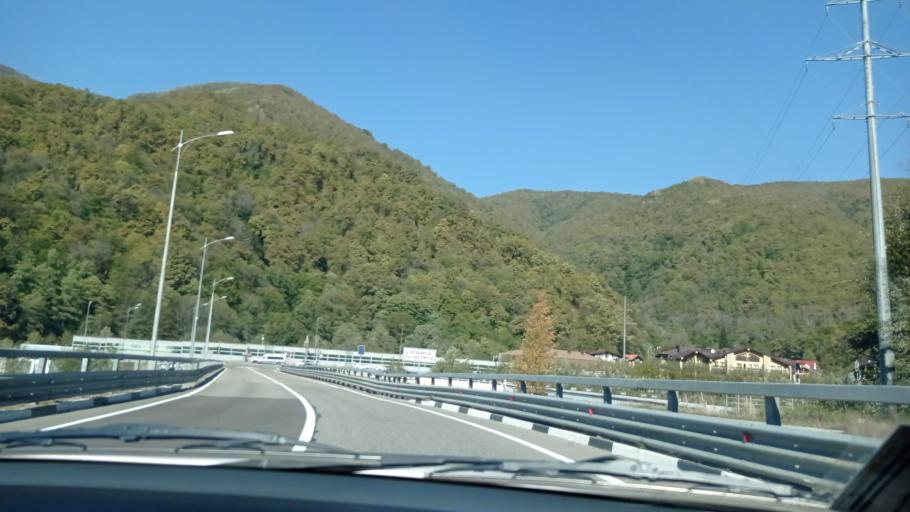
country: RU
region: Krasnodarskiy
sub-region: Sochi City
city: Krasnaya Polyana
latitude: 43.6851
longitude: 40.2460
